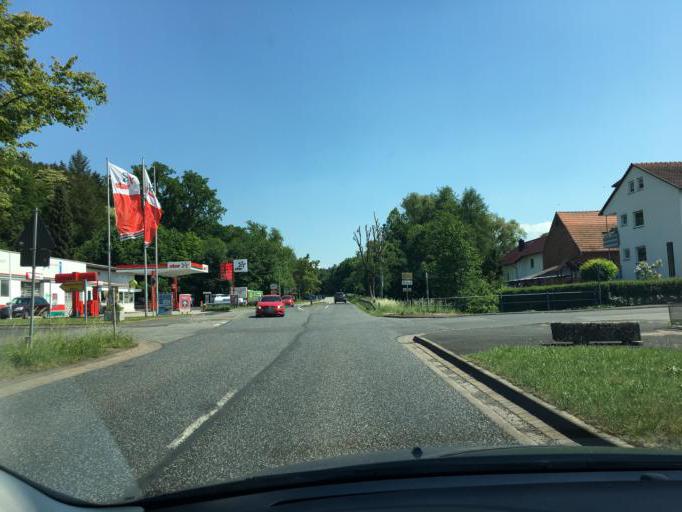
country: DE
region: Hesse
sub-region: Regierungsbezirk Kassel
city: Ronshausen
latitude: 50.9465
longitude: 9.8746
